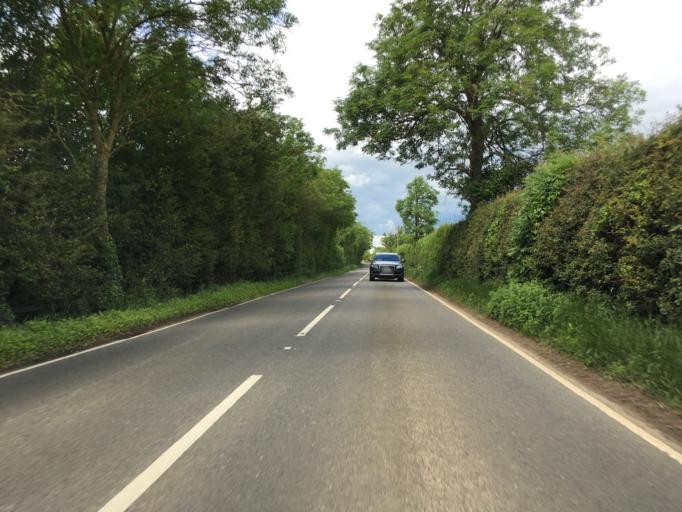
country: GB
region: England
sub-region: Northamptonshire
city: Brackley
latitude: 52.0787
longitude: -1.1403
